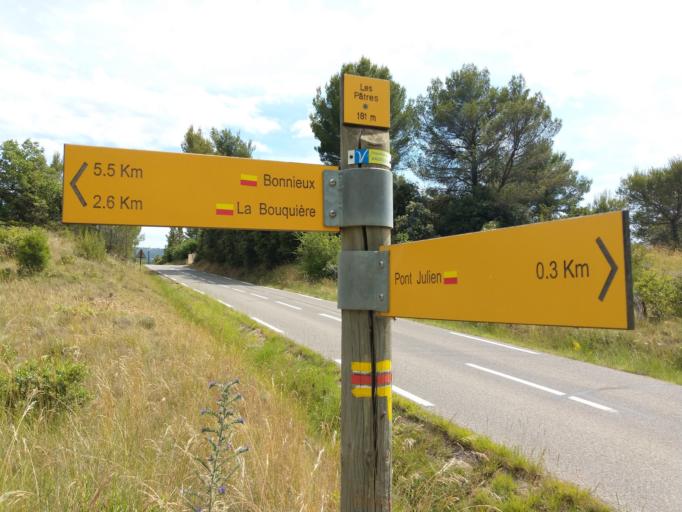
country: FR
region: Provence-Alpes-Cote d'Azur
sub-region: Departement du Vaucluse
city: Bonnieux
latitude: 43.8601
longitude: 5.3073
